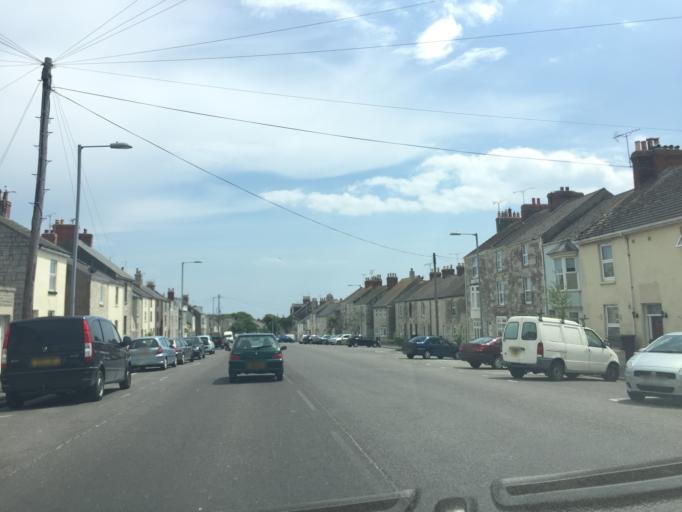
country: GB
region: England
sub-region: Dorset
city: Fortuneswell
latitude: 50.5443
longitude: -2.4330
